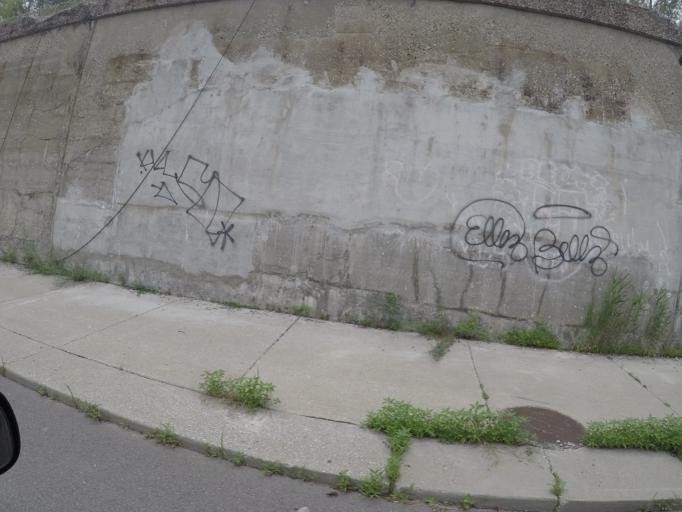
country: US
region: Michigan
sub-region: Wayne County
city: Detroit
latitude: 42.3287
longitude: -83.0789
